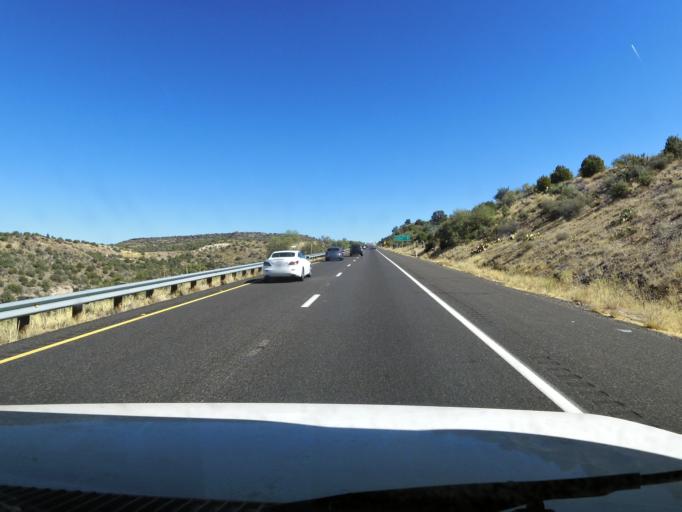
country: US
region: Arizona
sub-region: Yavapai County
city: Lake Montezuma
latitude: 34.7026
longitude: -111.7400
